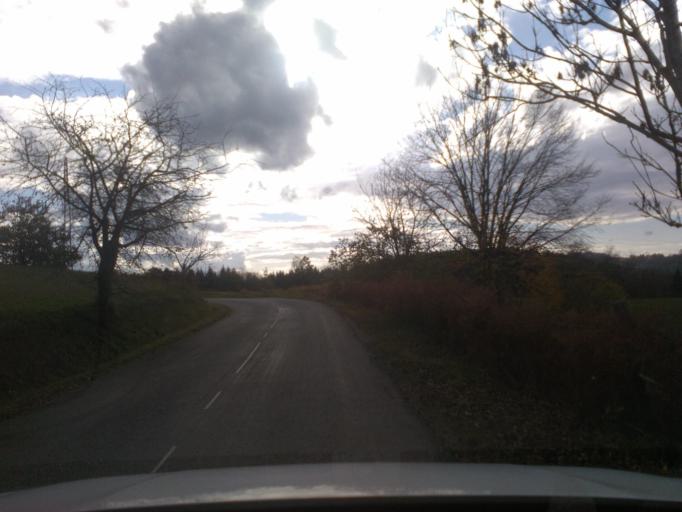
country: FR
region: Lorraine
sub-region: Departement des Vosges
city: Senones
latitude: 48.3735
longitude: 7.0008
